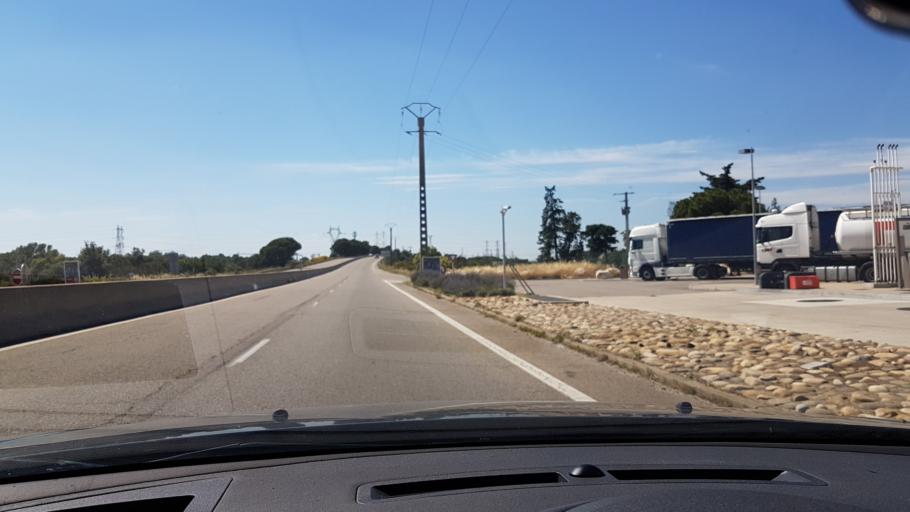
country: FR
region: Provence-Alpes-Cote d'Azur
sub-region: Departement des Bouches-du-Rhone
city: Fos-sur-Mer
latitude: 43.4714
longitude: 4.9077
